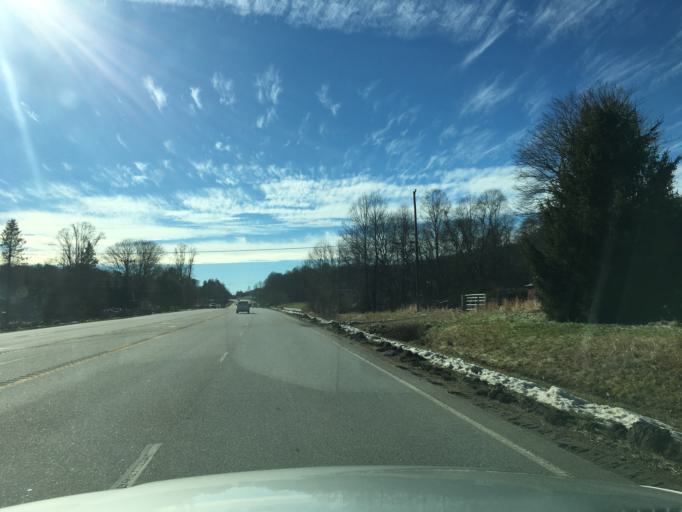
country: US
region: North Carolina
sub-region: Henderson County
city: Etowah
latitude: 35.3403
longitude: -82.6298
